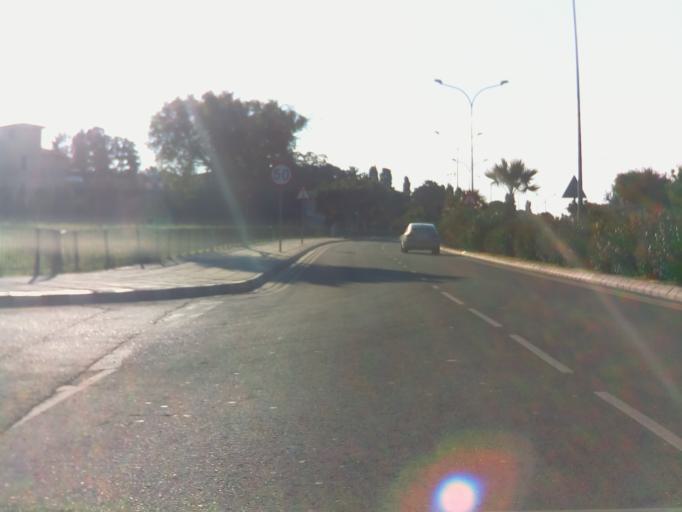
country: CY
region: Pafos
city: Paphos
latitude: 34.7591
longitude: 32.4231
